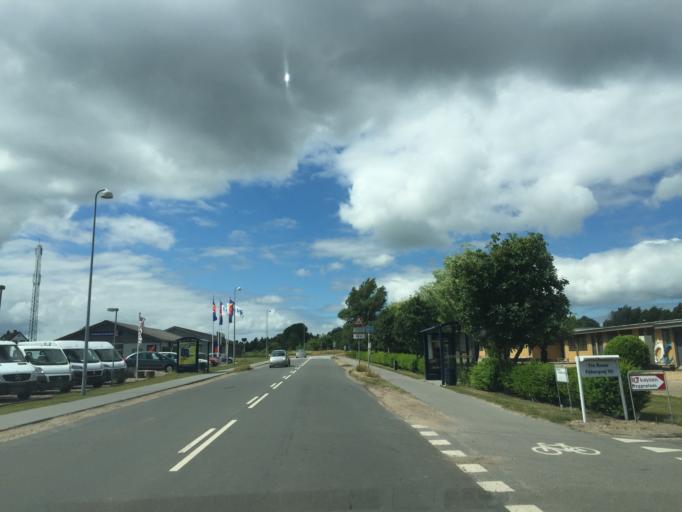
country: DK
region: South Denmark
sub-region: Svendborg Kommune
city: Svendborg
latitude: 55.0695
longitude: 10.5720
